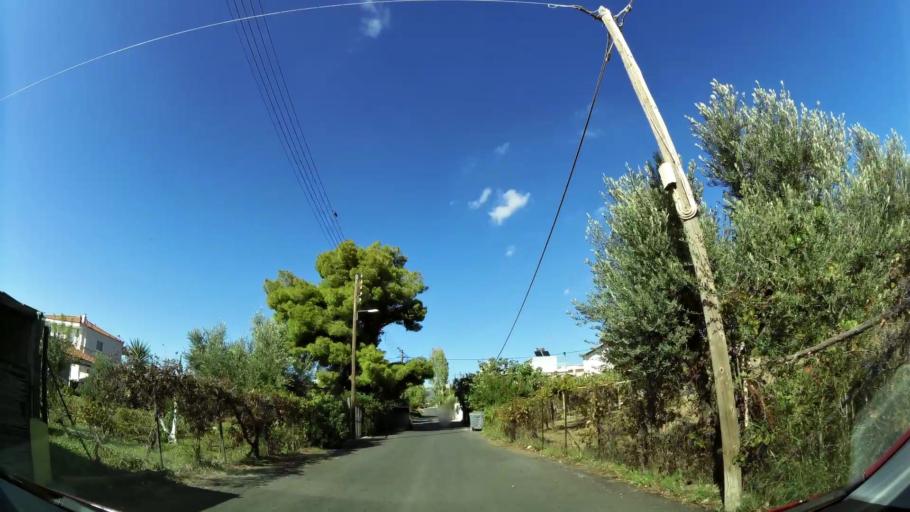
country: GR
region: Attica
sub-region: Nomarchia Anatolikis Attikis
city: Anthousa
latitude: 38.0138
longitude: 23.8753
